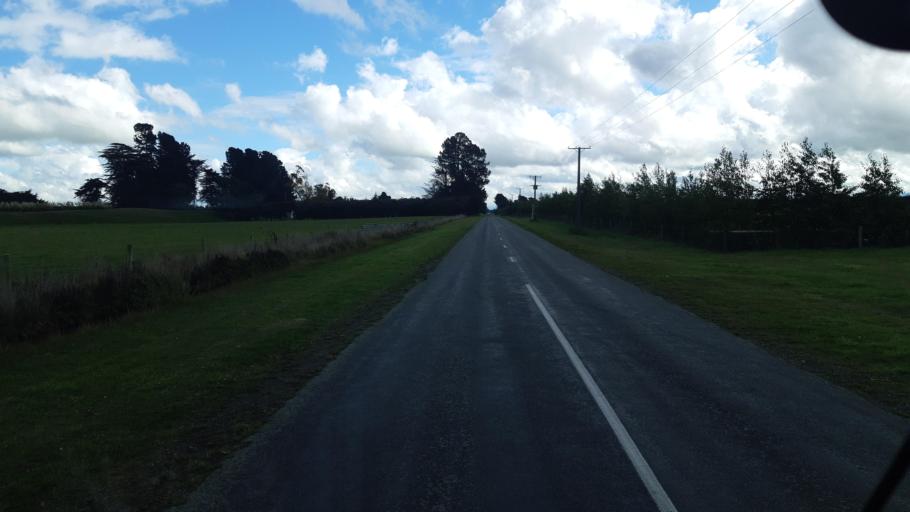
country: NZ
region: Canterbury
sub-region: Selwyn District
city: Rolleston
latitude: -43.5012
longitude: 172.3211
